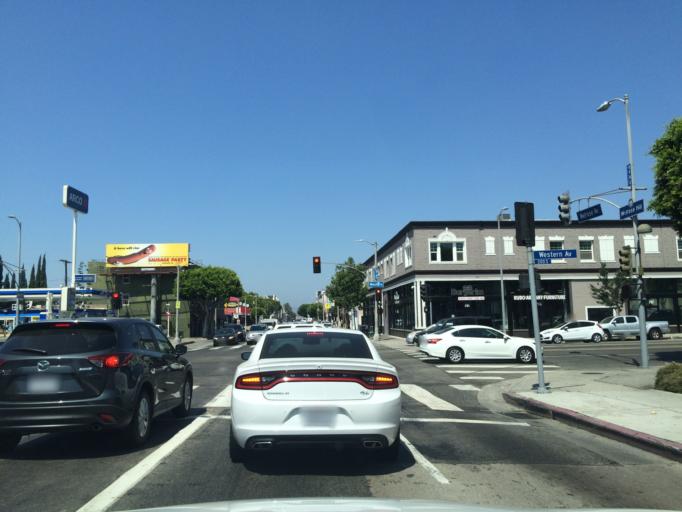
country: US
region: California
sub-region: Los Angeles County
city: Hollywood
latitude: 34.0836
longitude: -118.3088
